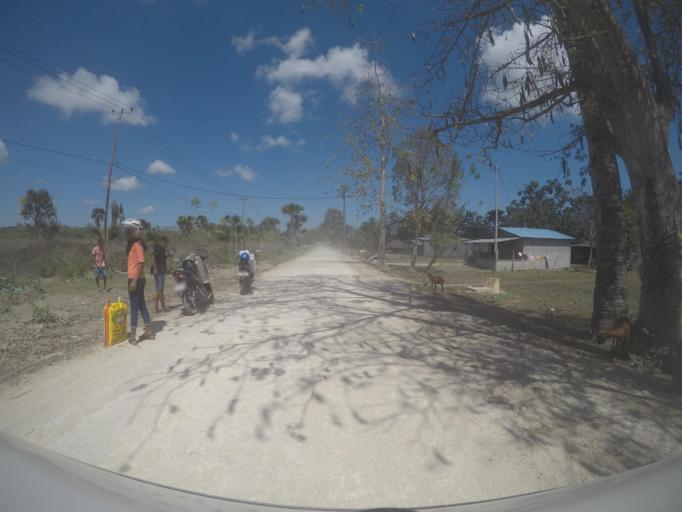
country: TL
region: Viqueque
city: Viqueque
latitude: -8.9250
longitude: 126.4043
